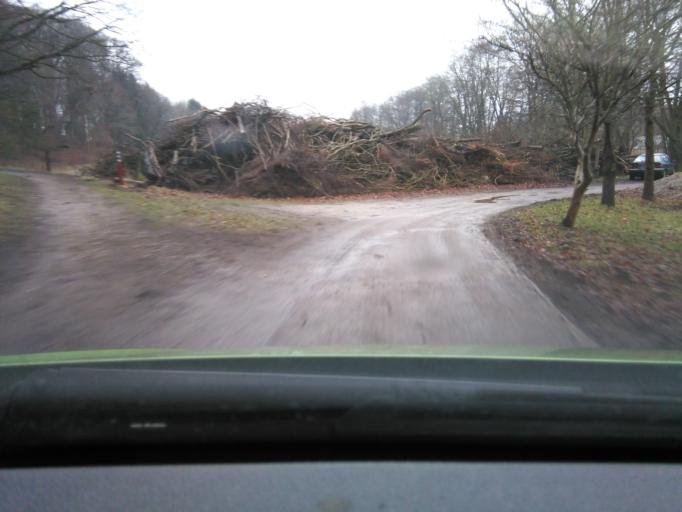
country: DK
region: Central Jutland
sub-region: Arhus Kommune
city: Beder
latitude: 56.0709
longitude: 10.2126
